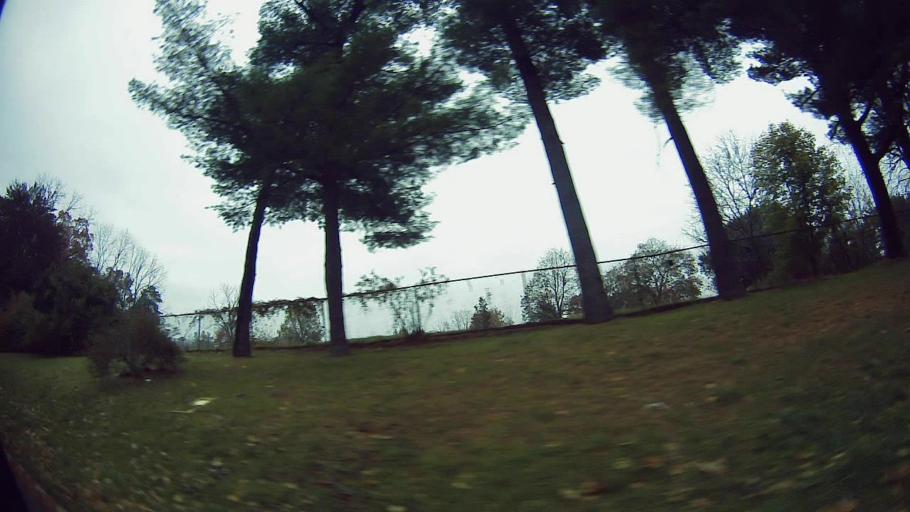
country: US
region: Michigan
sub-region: Wayne County
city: Dearborn Heights
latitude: 42.3630
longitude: -83.2604
